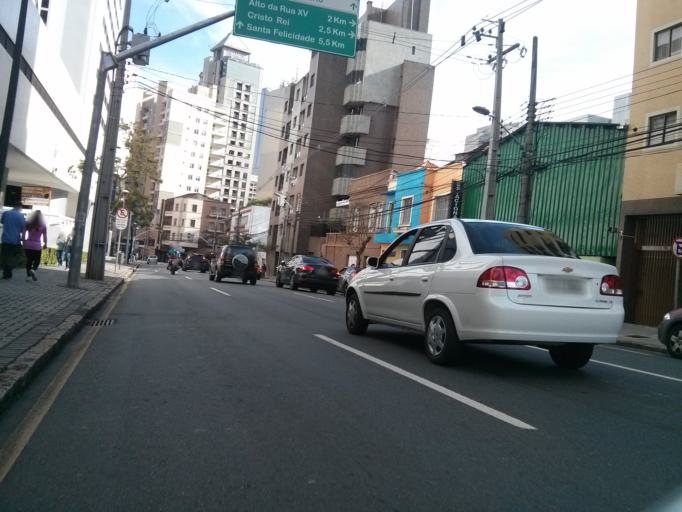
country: BR
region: Parana
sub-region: Curitiba
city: Curitiba
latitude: -25.4396
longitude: -49.2775
